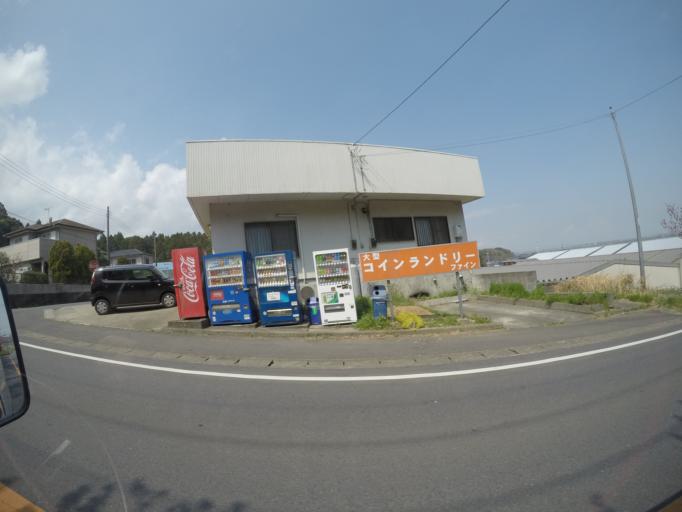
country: JP
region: Chiba
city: Omigawa
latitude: 35.8783
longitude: 140.5712
